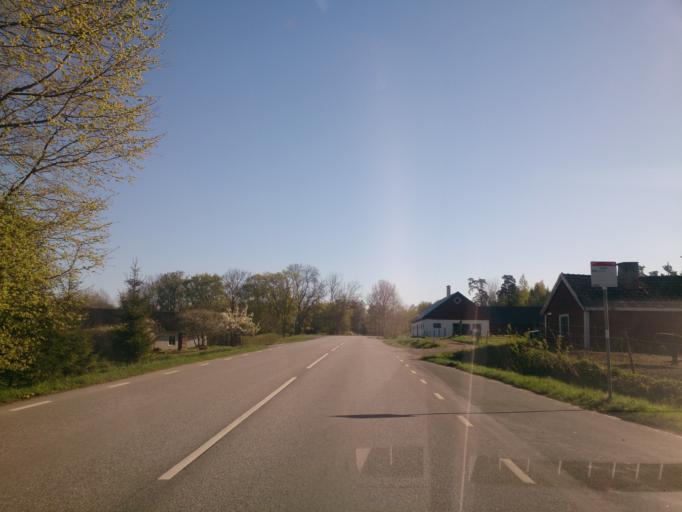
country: SE
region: OEstergoetland
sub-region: Linkopings Kommun
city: Berg
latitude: 58.5270
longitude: 15.5543
